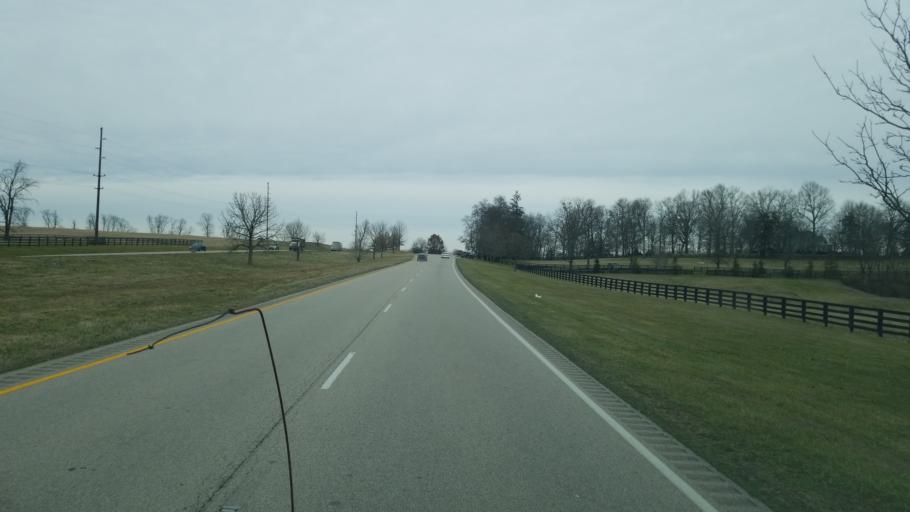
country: US
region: Kentucky
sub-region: Bourbon County
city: Paris
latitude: 38.1706
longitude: -84.3109
